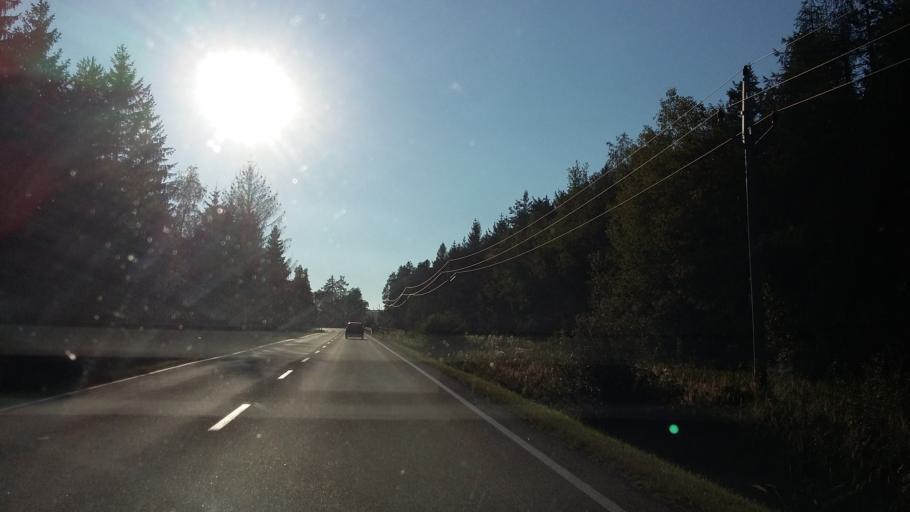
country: CZ
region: Vysocina
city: Kamenice
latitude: 49.4014
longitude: 15.8120
